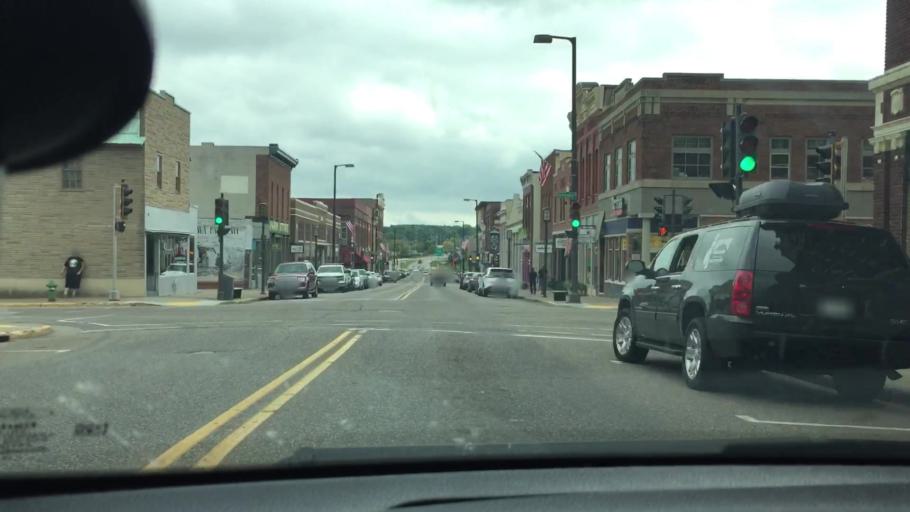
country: US
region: Wisconsin
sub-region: Chippewa County
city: Chippewa Falls
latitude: 44.9372
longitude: -91.3934
